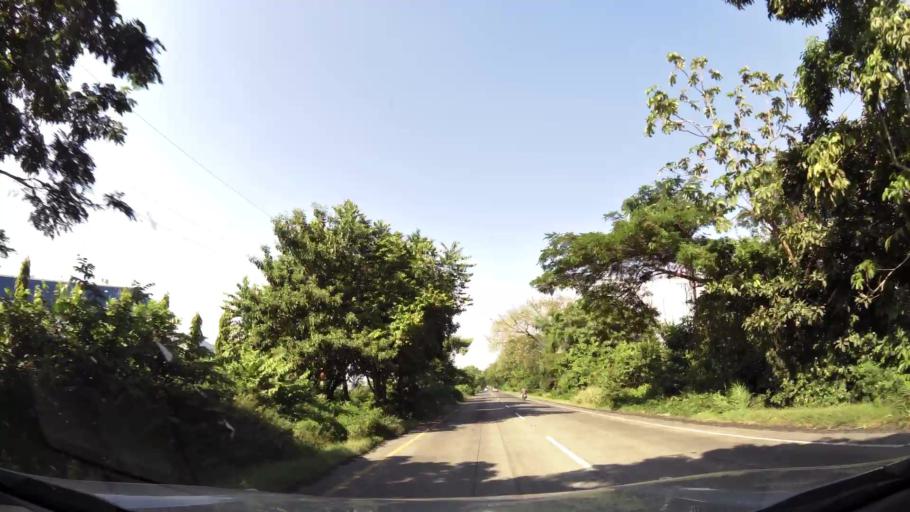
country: GT
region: Escuintla
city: Puerto San Jose
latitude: 13.9768
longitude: -90.7885
